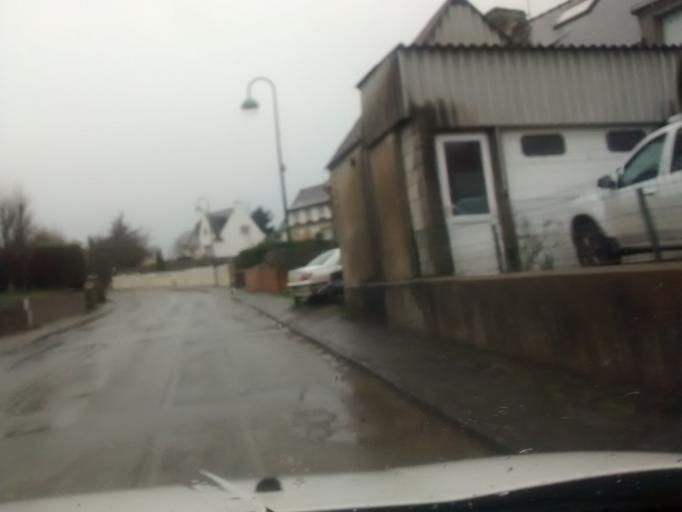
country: FR
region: Brittany
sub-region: Departement d'Ille-et-Vilaine
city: La Gouesniere
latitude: 48.5752
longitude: -1.8848
